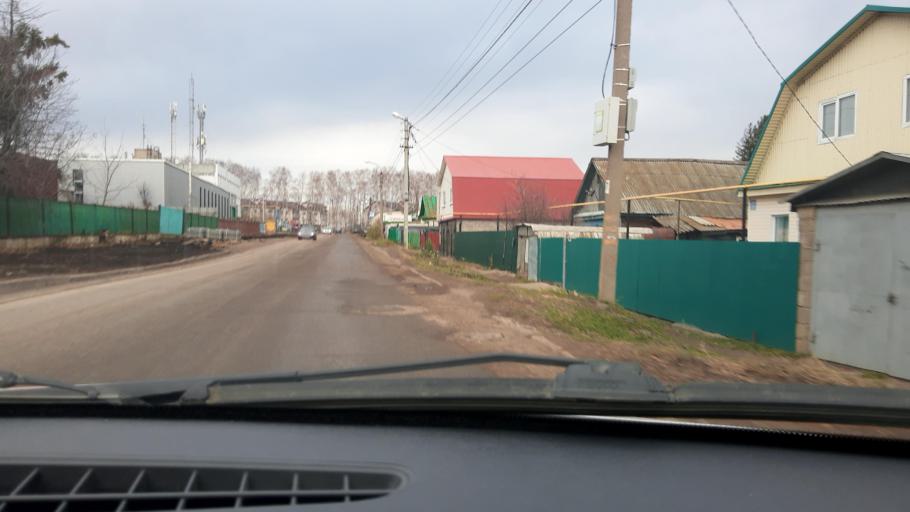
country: RU
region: Bashkortostan
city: Avdon
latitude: 54.6903
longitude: 55.7995
